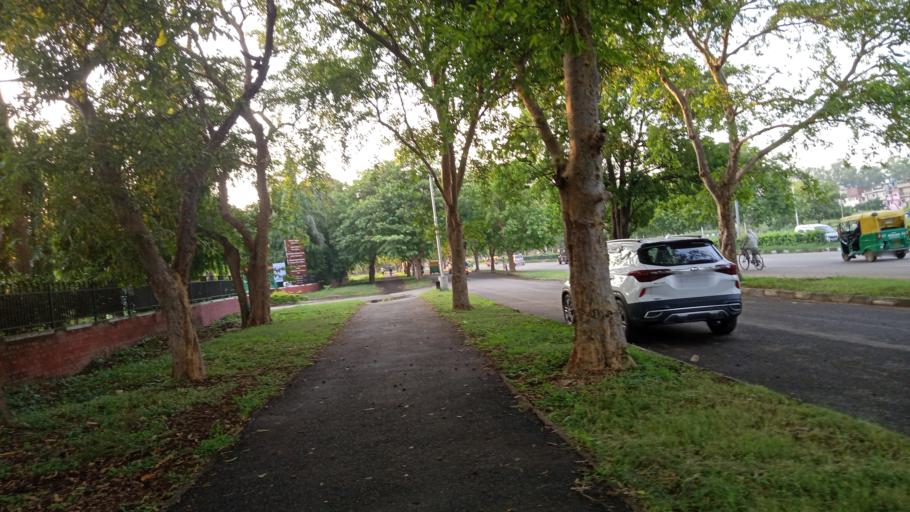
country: IN
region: Chandigarh
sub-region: Chandigarh
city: Chandigarh
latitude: 30.7483
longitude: 76.7510
